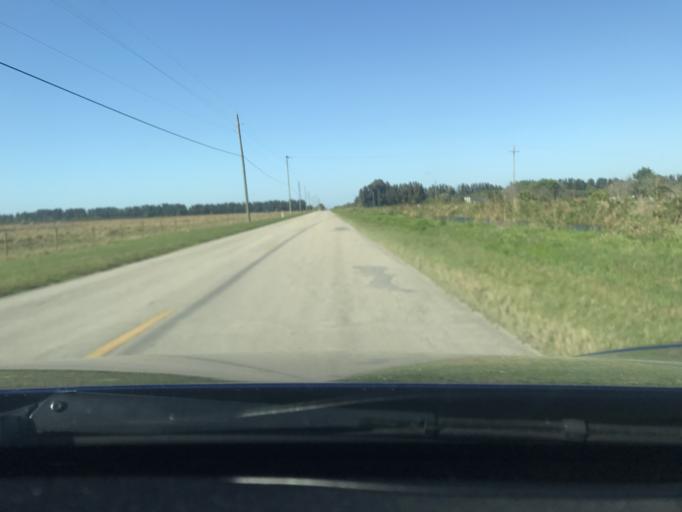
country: US
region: Florida
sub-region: Saint Lucie County
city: Lakewood Park
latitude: 27.4190
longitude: -80.4975
